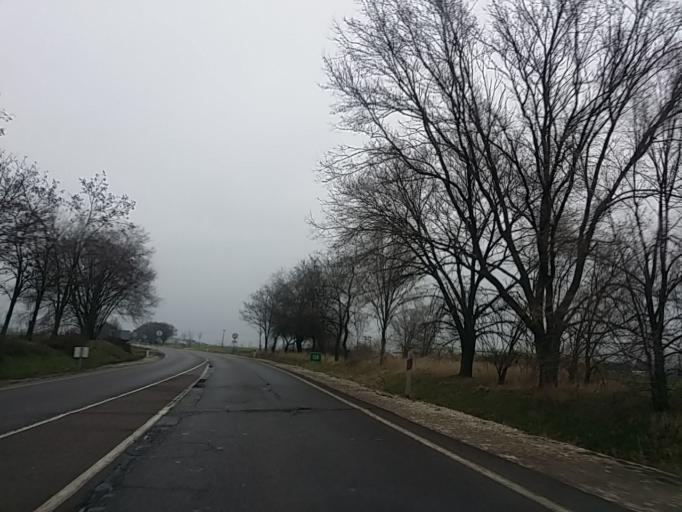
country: HU
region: Borsod-Abauj-Zemplen
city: Mezokovesd
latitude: 47.7995
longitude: 20.5402
